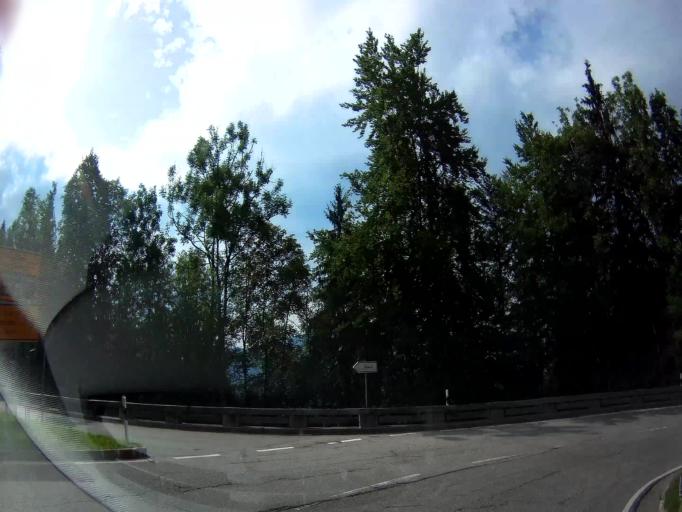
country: DE
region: Bavaria
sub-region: Upper Bavaria
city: Berchtesgaden
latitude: 47.6321
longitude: 13.0561
